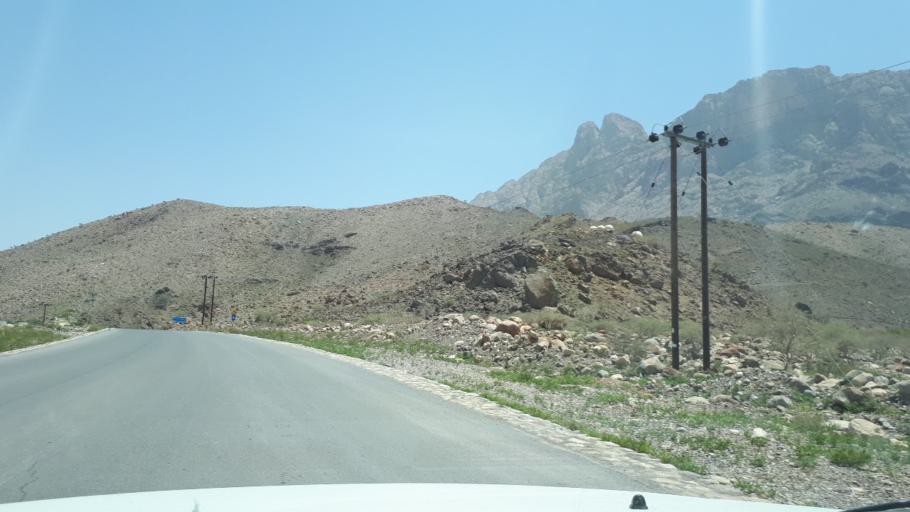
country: OM
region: Muhafazat ad Dakhiliyah
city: Bahla'
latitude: 23.1547
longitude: 57.1795
